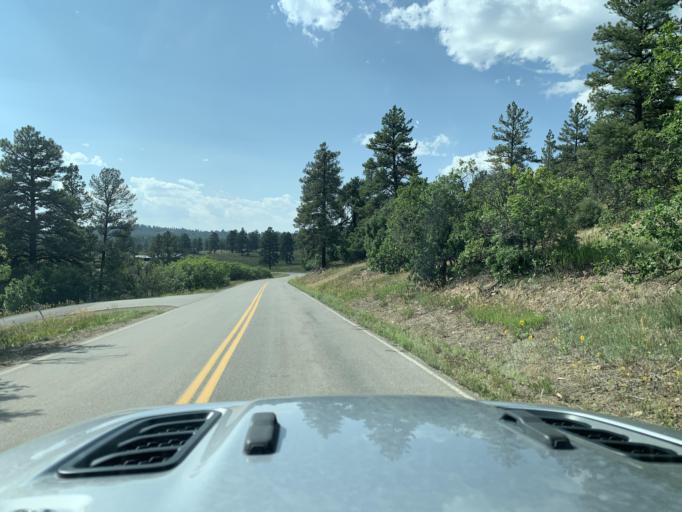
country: US
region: Colorado
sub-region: Archuleta County
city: Pagosa Springs
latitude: 37.2432
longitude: -107.0309
